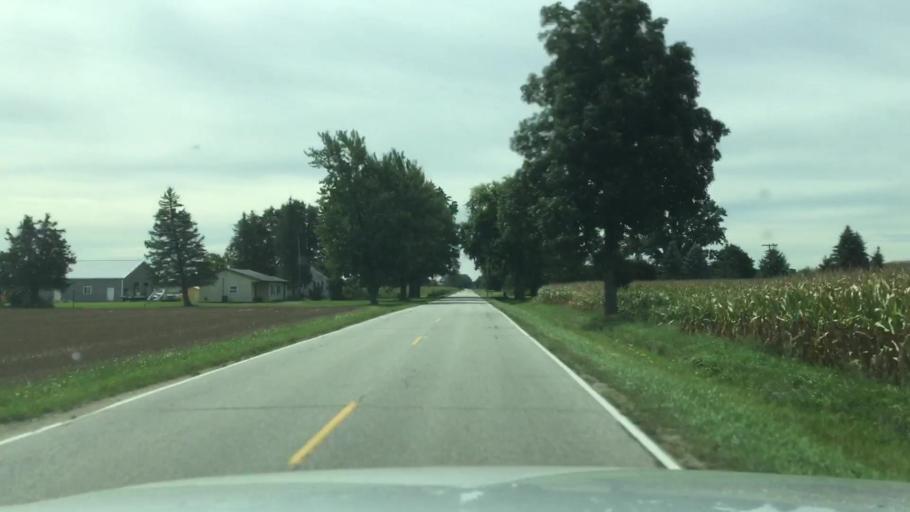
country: US
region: Michigan
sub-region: Genesee County
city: Montrose
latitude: 43.1256
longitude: -83.9880
